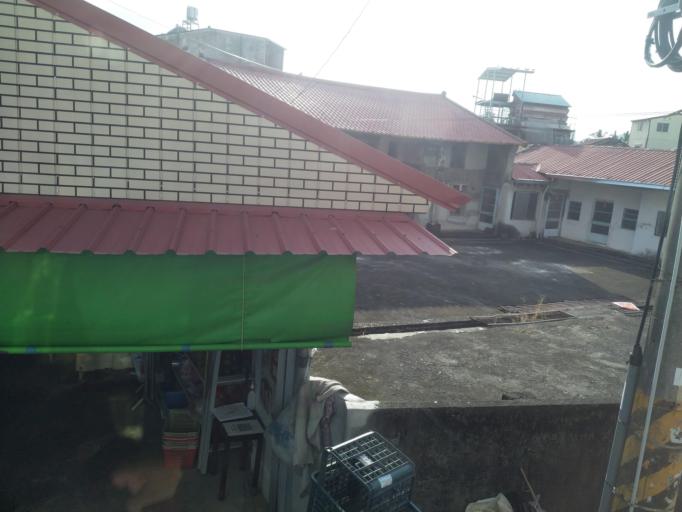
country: TW
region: Taiwan
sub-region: Pingtung
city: Pingtung
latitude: 22.8972
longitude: 120.5433
